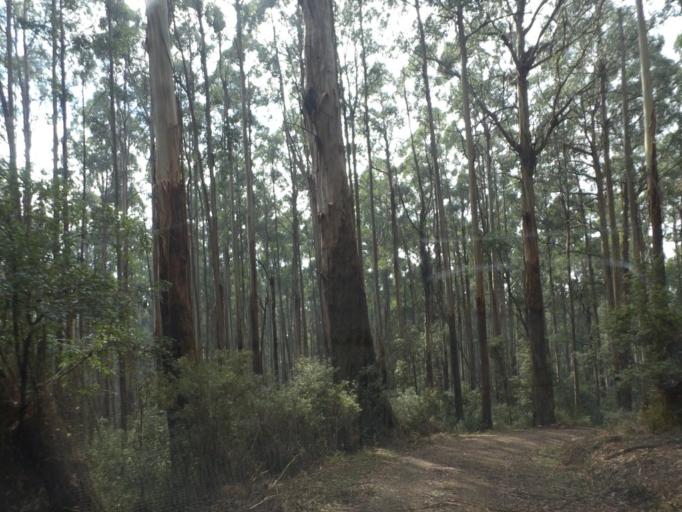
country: AU
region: Victoria
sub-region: Yarra Ranges
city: Healesville
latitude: -37.5711
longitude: 145.6145
